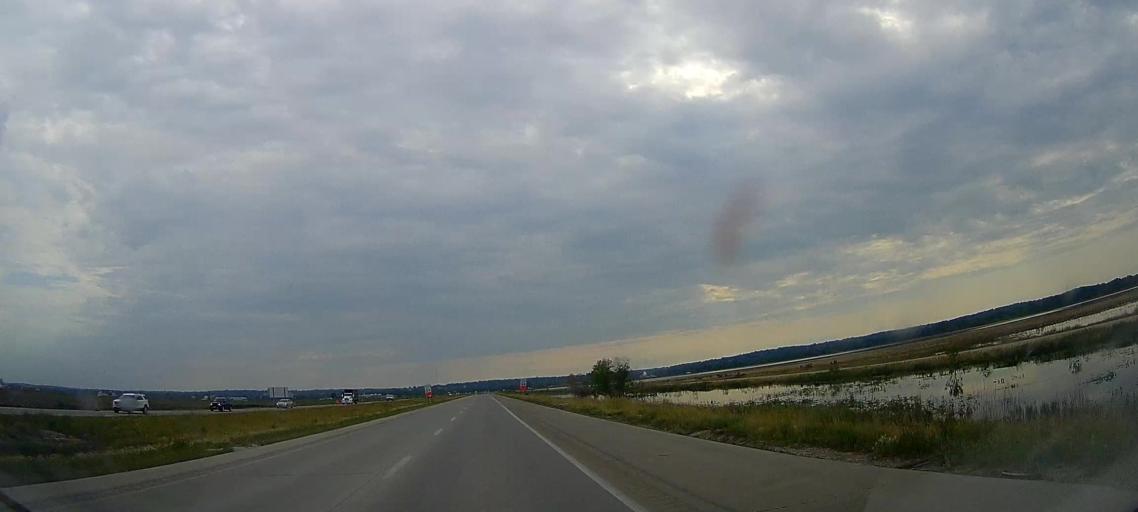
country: US
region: Iowa
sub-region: Pottawattamie County
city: Carter Lake
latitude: 41.3506
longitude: -95.9133
